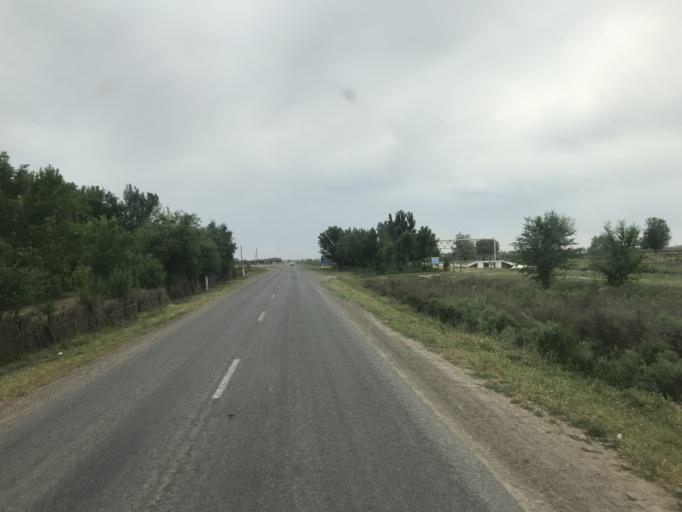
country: KZ
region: Ongtustik Qazaqstan
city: Asykata
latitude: 40.9263
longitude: 68.4038
